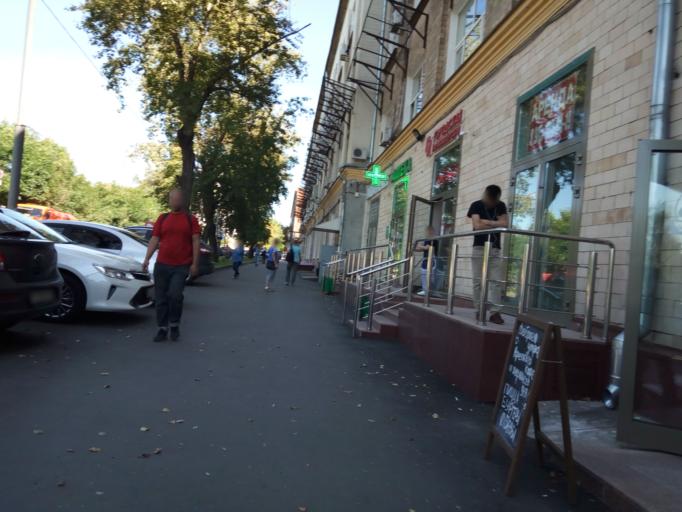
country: RU
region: Moscow
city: Sokol
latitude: 55.7741
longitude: 37.5200
